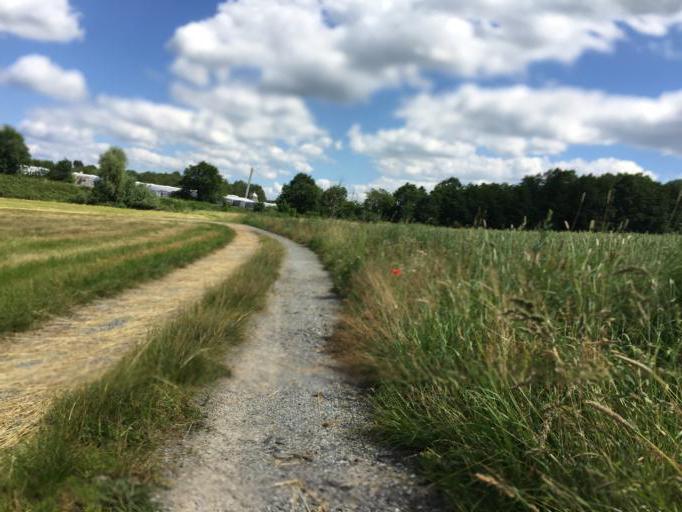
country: DE
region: Rheinland-Pfalz
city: Bannberscheid
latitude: 50.4647
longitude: 7.8387
